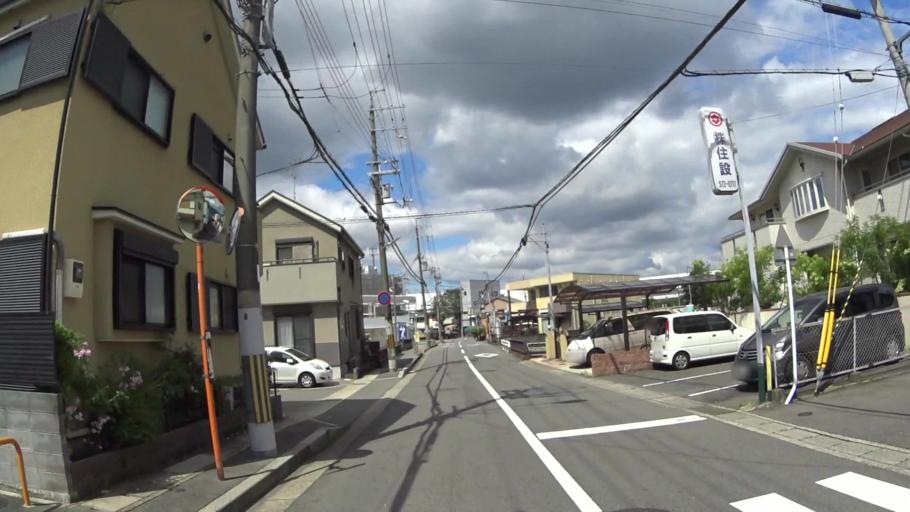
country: JP
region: Shiga Prefecture
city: Otsu-shi
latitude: 34.9631
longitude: 135.8142
